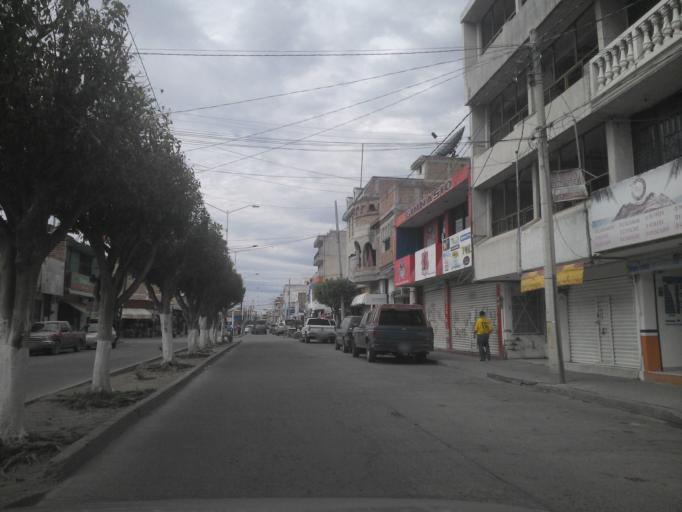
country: MX
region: Guanajuato
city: San Francisco del Rincon
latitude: 21.0133
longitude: -101.8574
